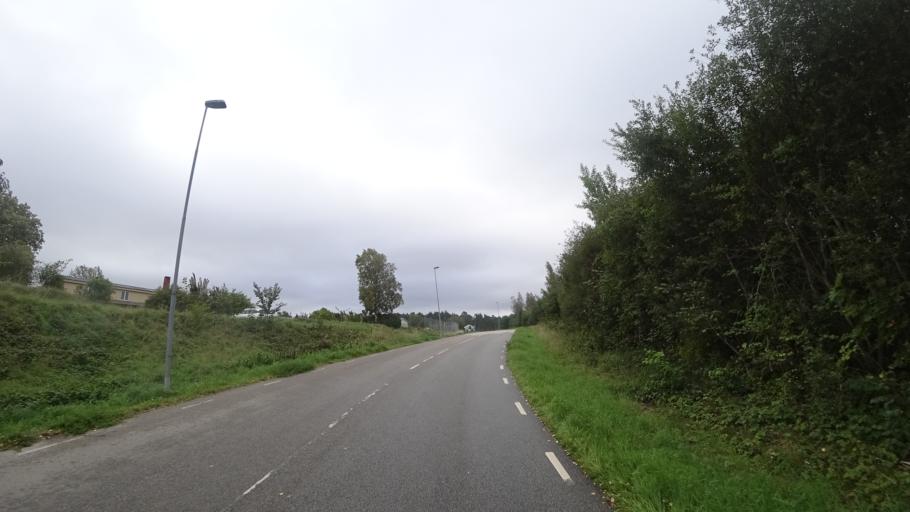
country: SE
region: Skane
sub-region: Kavlinge Kommun
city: Kaevlinge
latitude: 55.7850
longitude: 13.1113
